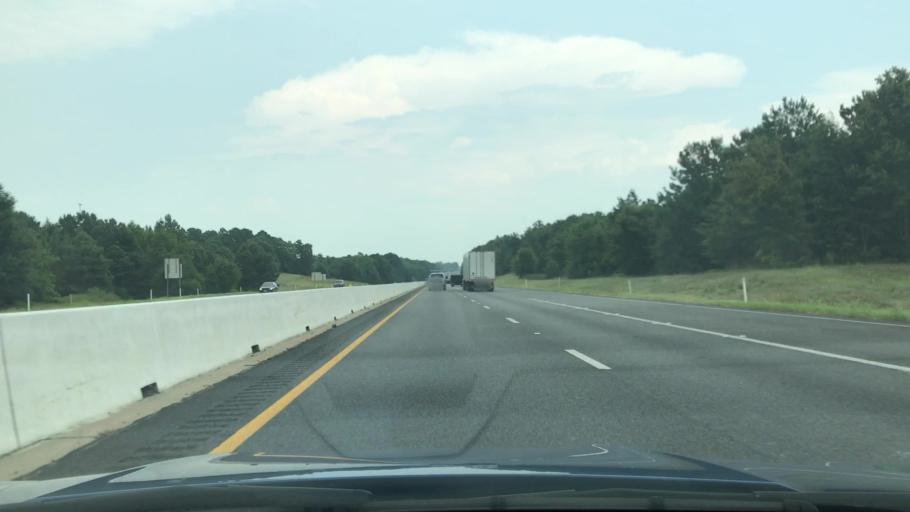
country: US
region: Texas
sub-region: Gregg County
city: Liberty City
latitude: 32.4362
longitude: -94.9854
